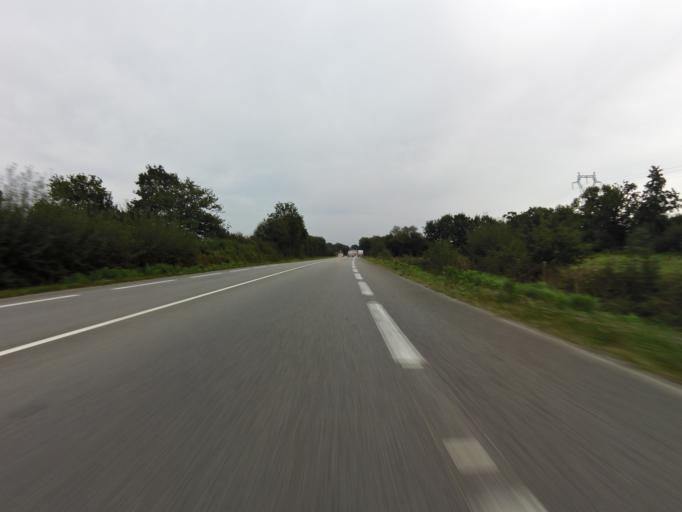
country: FR
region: Brittany
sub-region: Departement du Morbihan
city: Plescop
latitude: 47.7008
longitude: -2.7908
